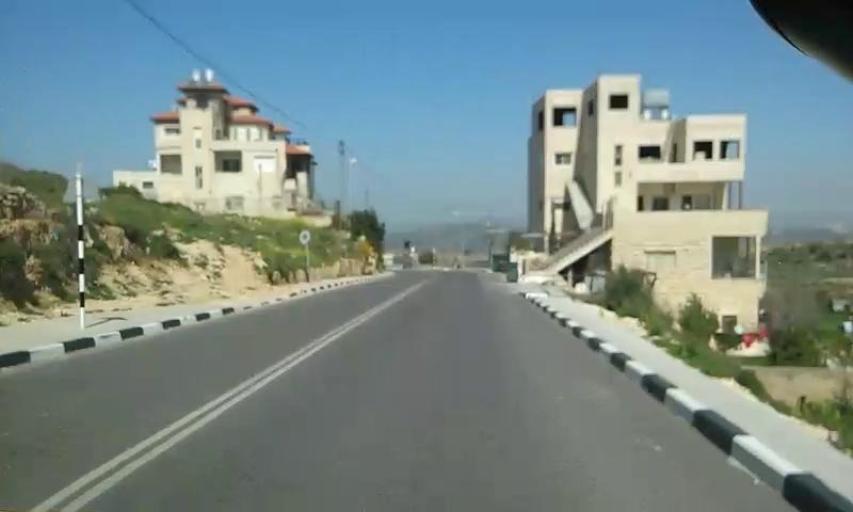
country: PS
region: West Bank
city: Husan
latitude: 31.7074
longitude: 35.1486
